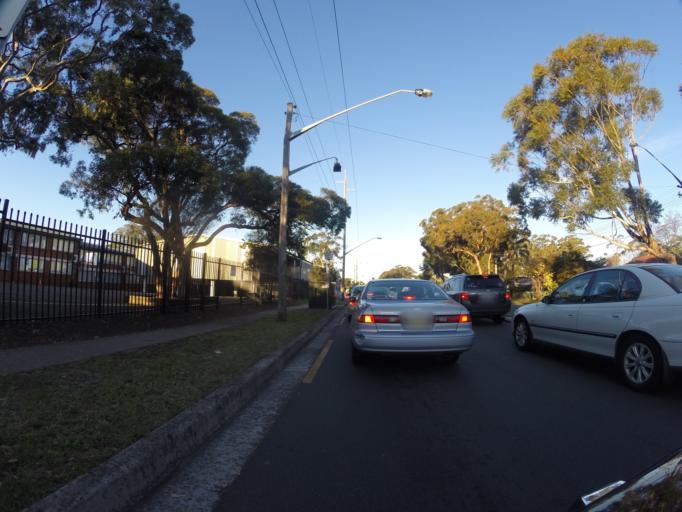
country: AU
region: New South Wales
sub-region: Sutherland Shire
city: Gymea
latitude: -34.0375
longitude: 151.0834
